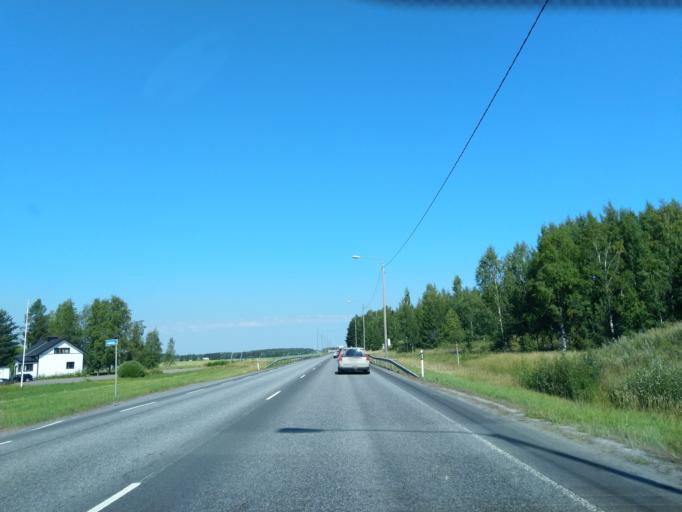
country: FI
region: Satakunta
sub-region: Pori
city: Nakkila
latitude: 61.3658
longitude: 21.9881
